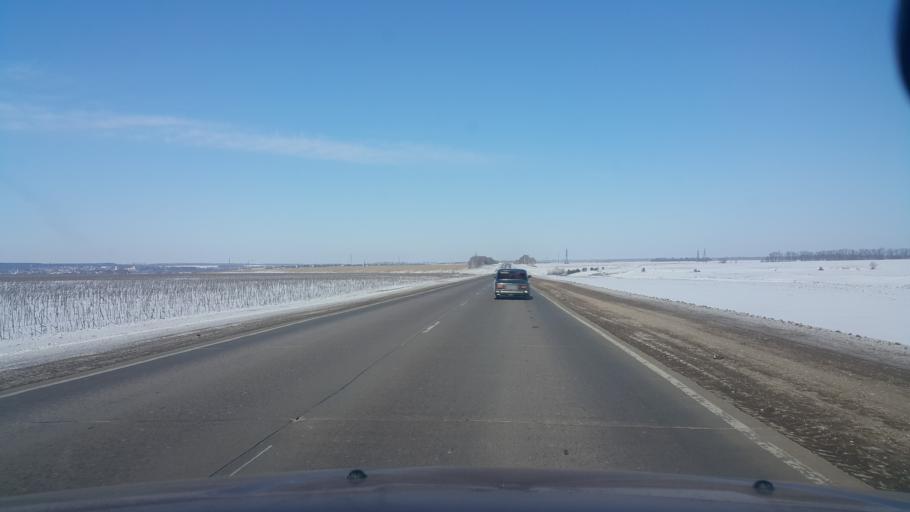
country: RU
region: Tambov
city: Pokrovo-Prigorodnoye
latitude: 52.6259
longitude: 41.3427
